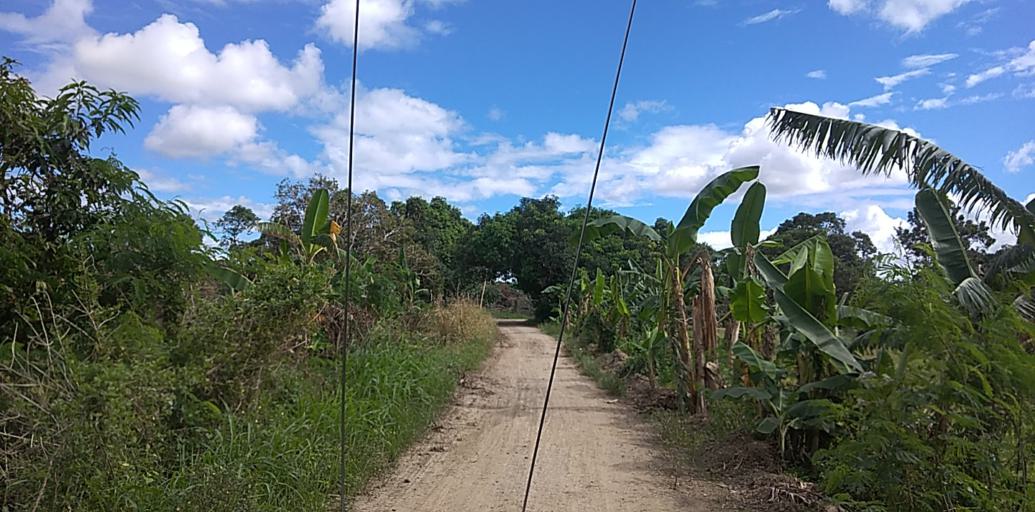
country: PH
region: Central Luzon
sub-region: Province of Pampanga
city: Santa Ana
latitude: 15.1174
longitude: 120.7805
